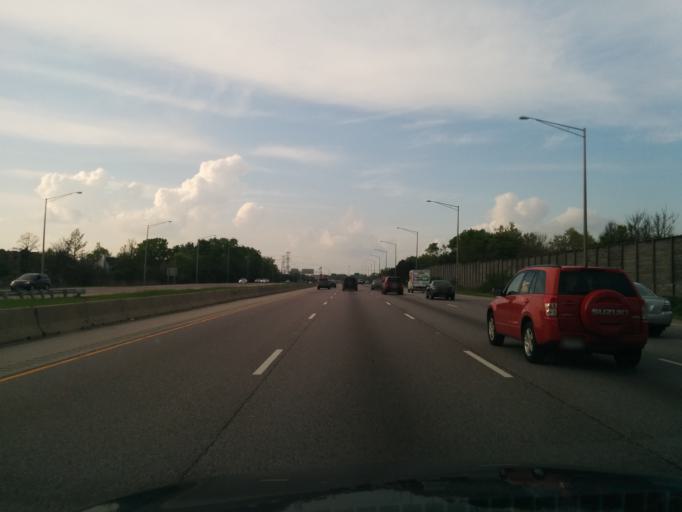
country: US
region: Illinois
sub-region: DuPage County
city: Glendale Heights
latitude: 41.9372
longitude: -88.0375
